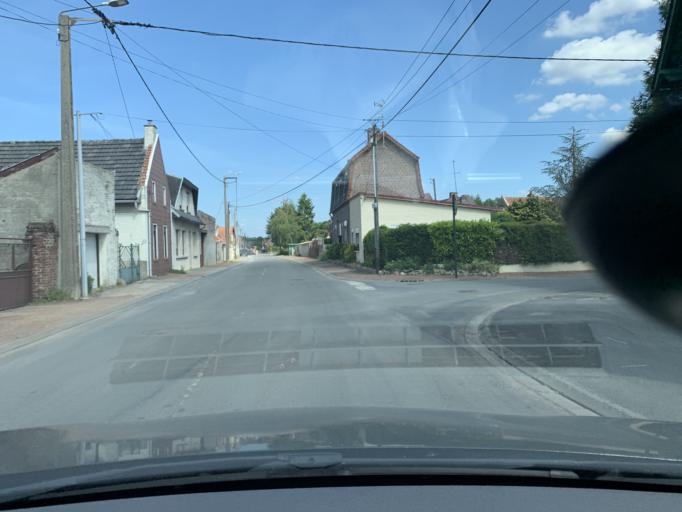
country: FR
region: Nord-Pas-de-Calais
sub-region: Departement du Pas-de-Calais
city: Oisy-le-Verger
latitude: 50.2362
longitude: 3.0996
